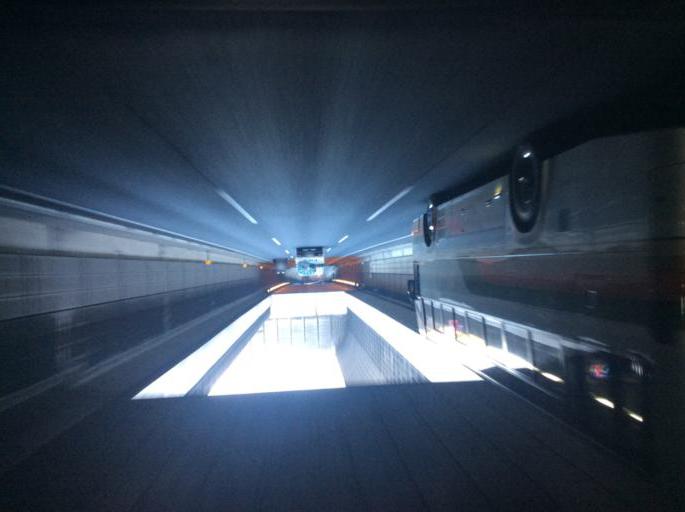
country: JP
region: Chiba
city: Nagareyama
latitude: 35.8990
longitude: 139.9246
